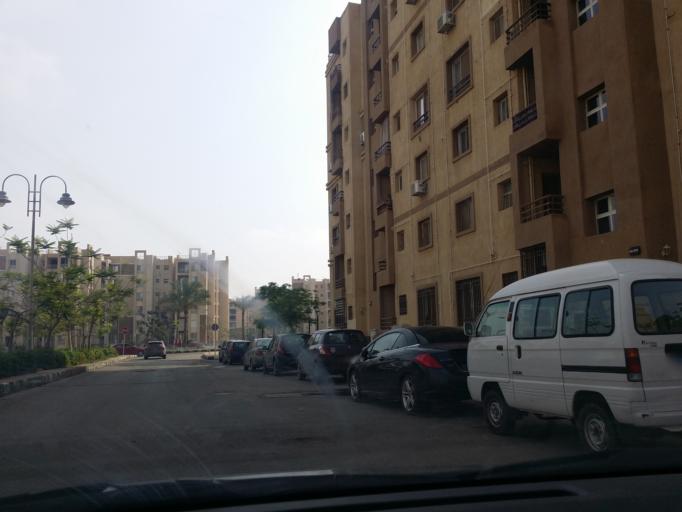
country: EG
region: Muhafazat al Qalyubiyah
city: Al Khankah
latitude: 30.0835
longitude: 31.6460
